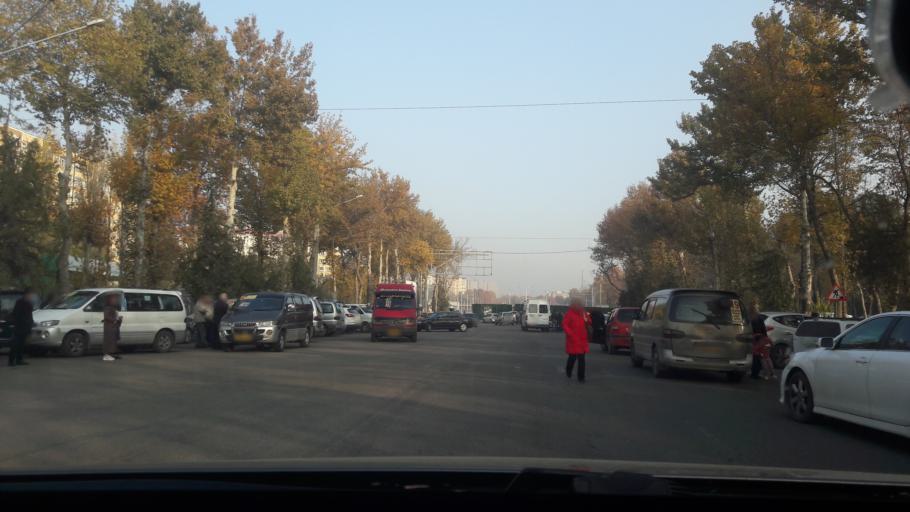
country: TJ
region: Dushanbe
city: Dushanbe
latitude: 38.5801
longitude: 68.7551
